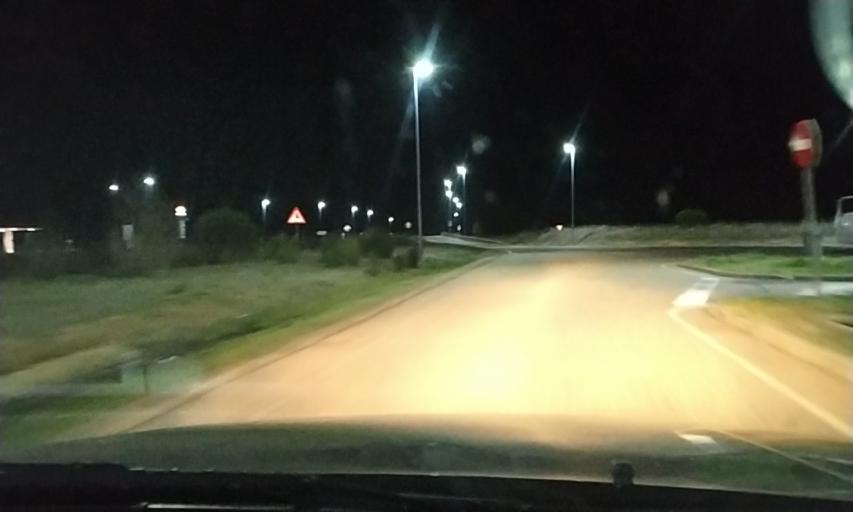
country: ES
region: Castille and Leon
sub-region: Provincia de Zamora
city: Pobladura del Valle
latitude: 42.0885
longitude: -5.7150
